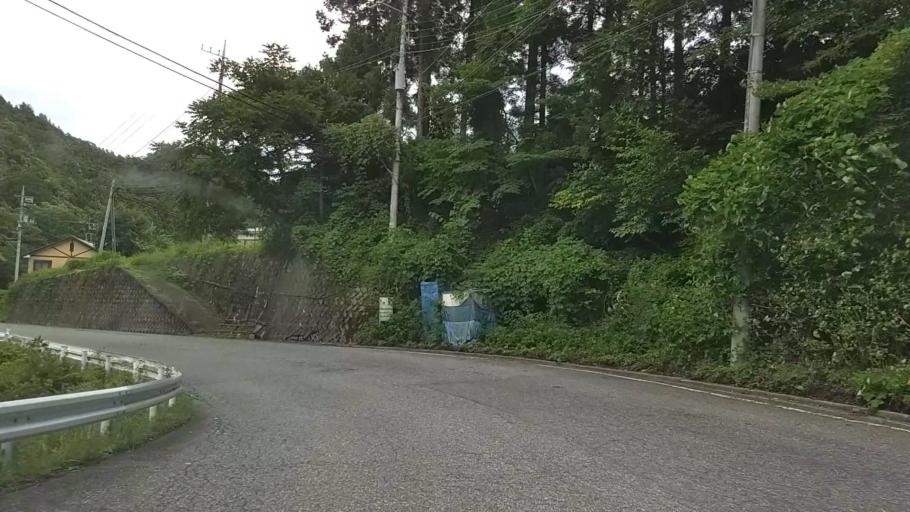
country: JP
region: Yamanashi
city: Uenohara
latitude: 35.5769
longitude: 139.0542
